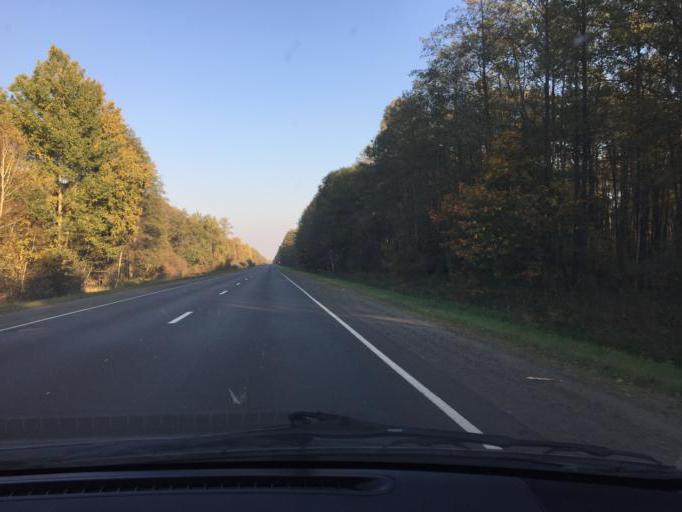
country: BY
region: Brest
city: Mikashevichy
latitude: 52.2439
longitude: 27.3482
